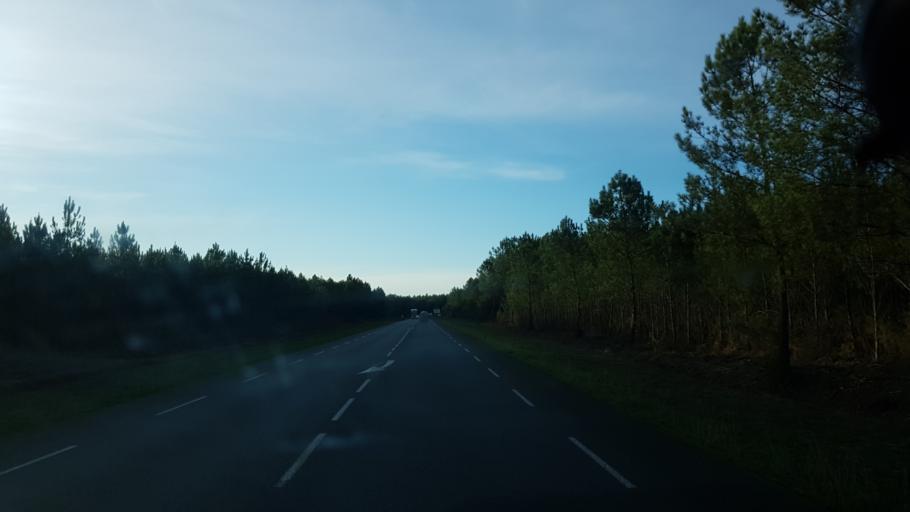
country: FR
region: Aquitaine
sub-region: Departement de la Gironde
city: Martignas-sur-Jalle
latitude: 44.8327
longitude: -0.7970
